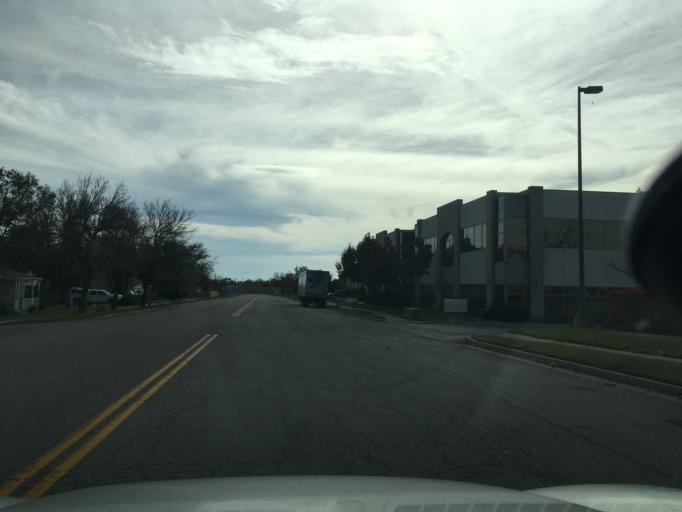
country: US
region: Utah
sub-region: Davis County
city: Layton
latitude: 41.0739
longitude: -111.9735
